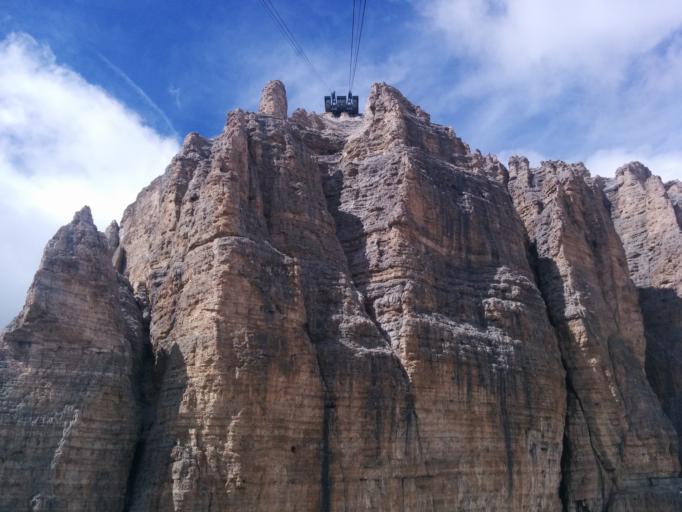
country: IT
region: Trentino-Alto Adige
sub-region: Provincia di Trento
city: Canazei
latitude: 46.4980
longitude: 11.8085
